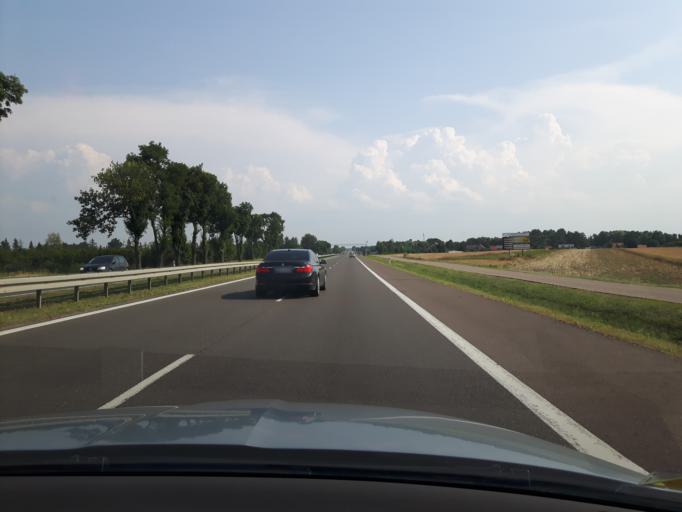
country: PL
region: Masovian Voivodeship
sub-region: Powiat plonski
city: Zaluski
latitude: 52.5725
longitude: 20.4837
